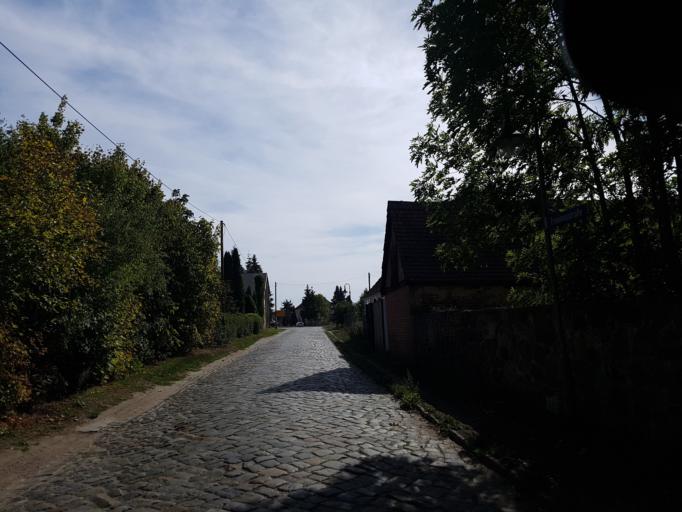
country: DE
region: Saxony-Anhalt
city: Lindau
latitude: 52.0280
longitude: 12.2251
